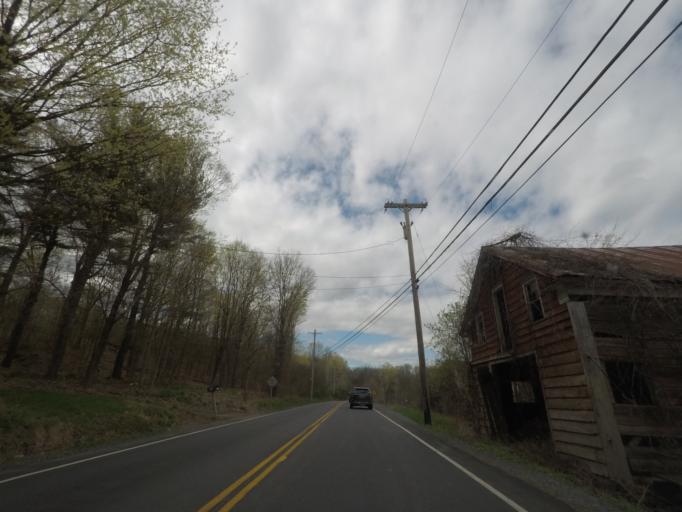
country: US
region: New York
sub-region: Columbia County
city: Valatie
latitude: 42.3841
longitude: -73.6413
